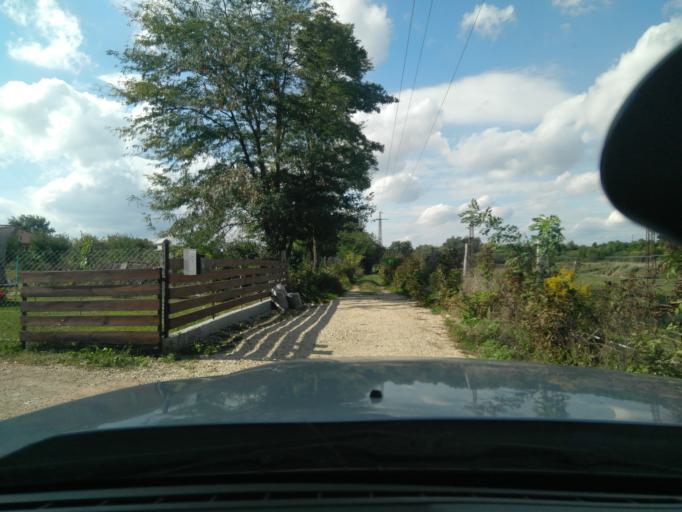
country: HU
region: Fejer
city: Bicske
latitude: 47.4857
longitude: 18.6545
